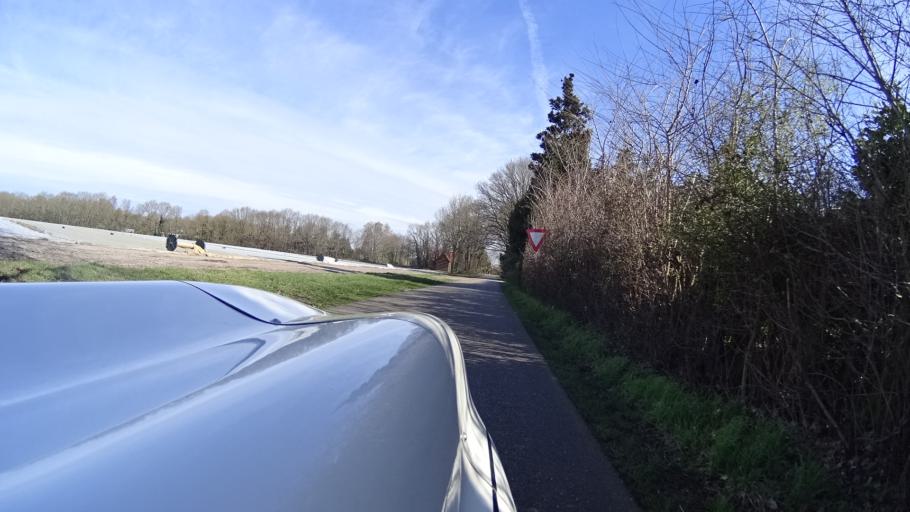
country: NL
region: North Brabant
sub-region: Gemeente Mill en Sint Hubert
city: Wilbertoord
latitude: 51.7001
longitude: 5.7633
